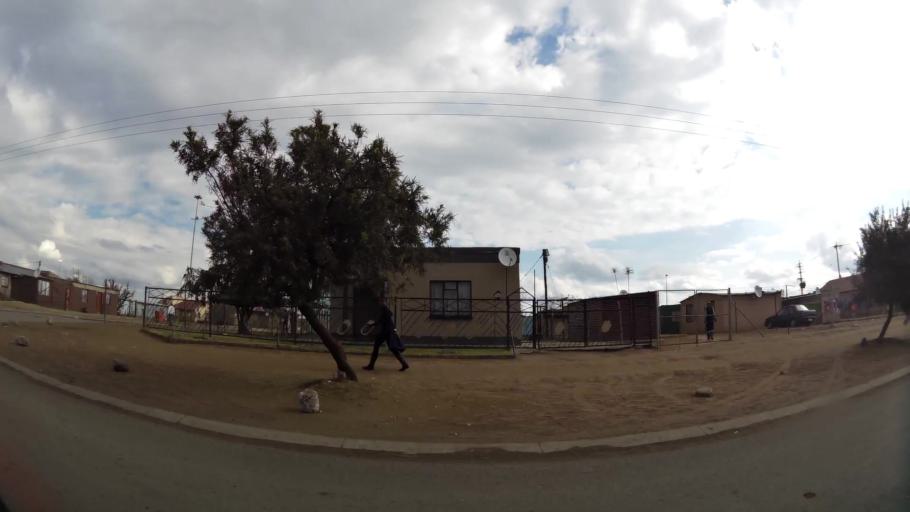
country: ZA
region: Gauteng
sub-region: Sedibeng District Municipality
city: Vanderbijlpark
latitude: -26.6841
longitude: 27.7824
